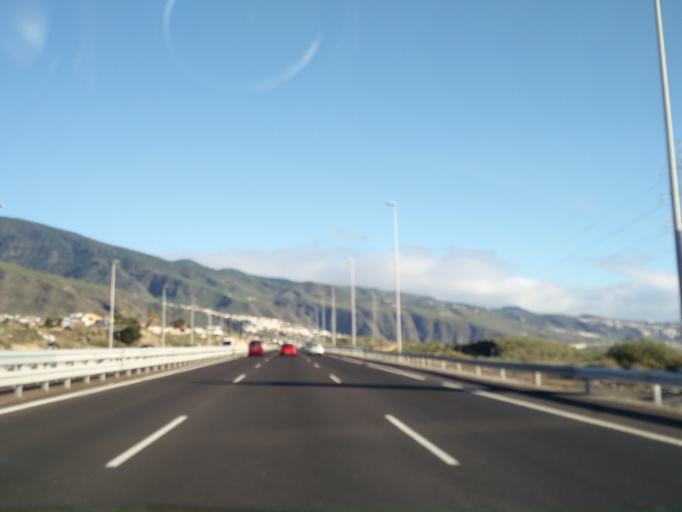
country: ES
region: Canary Islands
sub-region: Provincia de Santa Cruz de Tenerife
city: Candelaria
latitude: 28.3431
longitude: -16.3738
